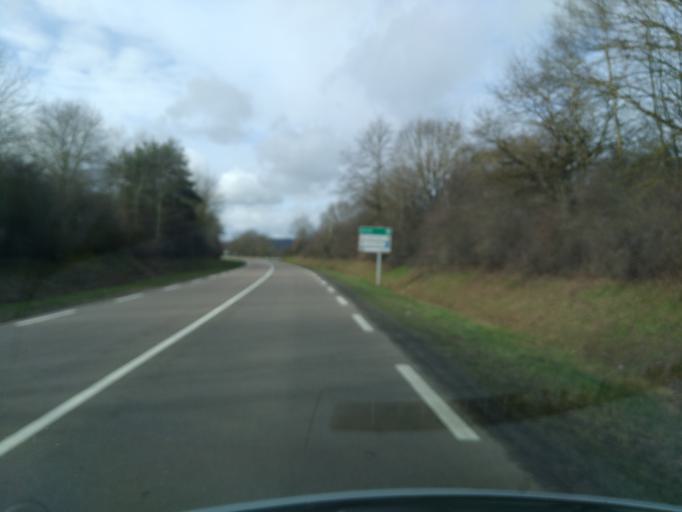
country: FR
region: Bourgogne
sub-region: Departement de Saone-et-Loire
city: Torcy
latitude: 46.7719
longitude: 4.4295
